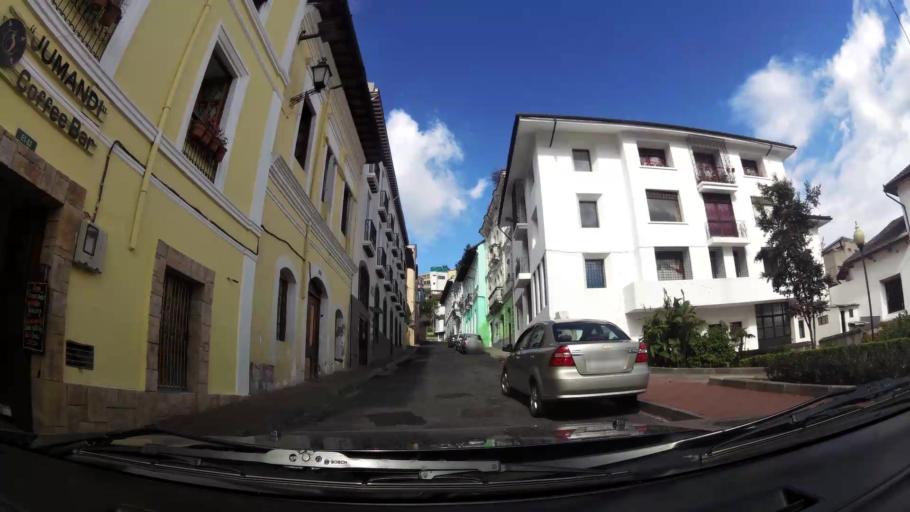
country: EC
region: Pichincha
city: Quito
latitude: -0.2178
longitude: -78.5048
